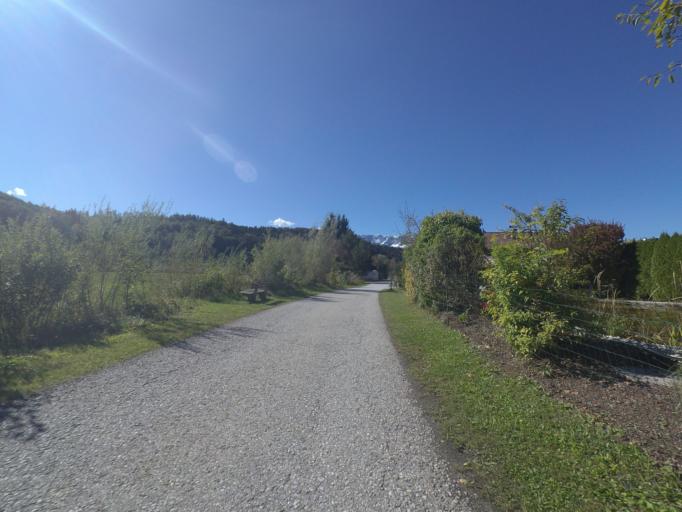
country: AT
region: Salzburg
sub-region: Politischer Bezirk Hallein
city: Adnet
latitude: 47.6947
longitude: 13.1322
